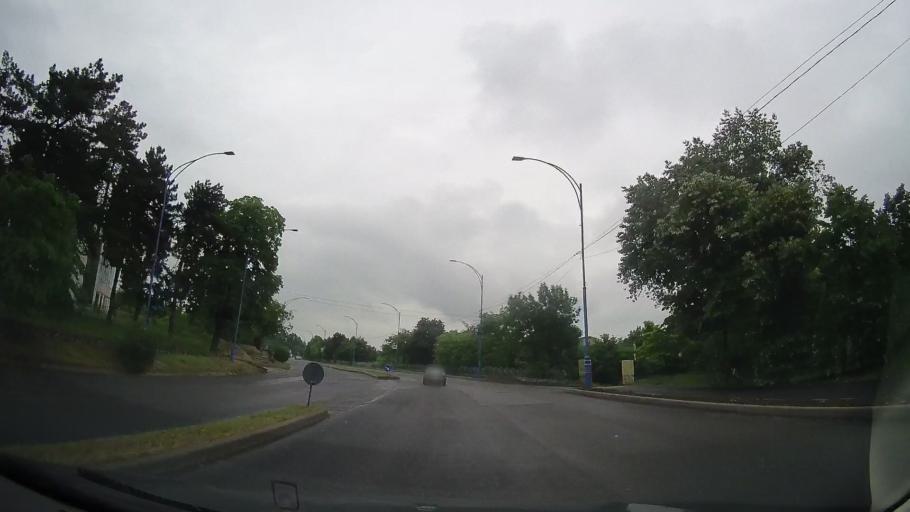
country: RO
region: Mehedinti
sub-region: Municipiul Drobeta-Turnu Severin
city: Drobeta-Turnu Severin
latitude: 44.6256
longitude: 22.6392
